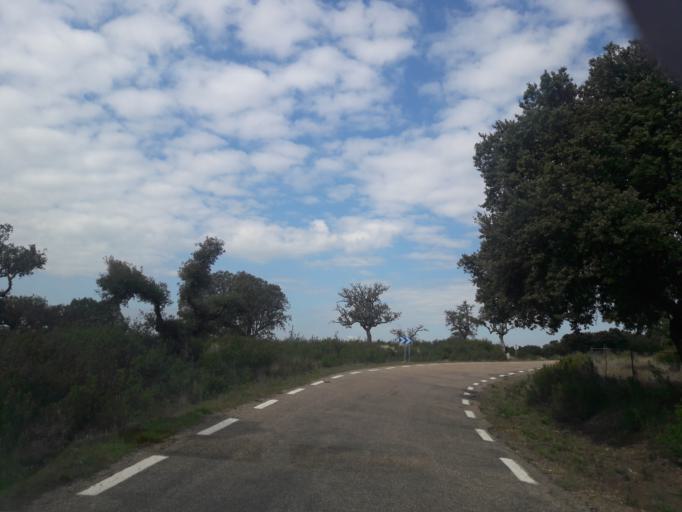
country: ES
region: Castille and Leon
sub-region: Provincia de Salamanca
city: Serradilla del Arroyo
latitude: 40.5407
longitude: -6.4012
